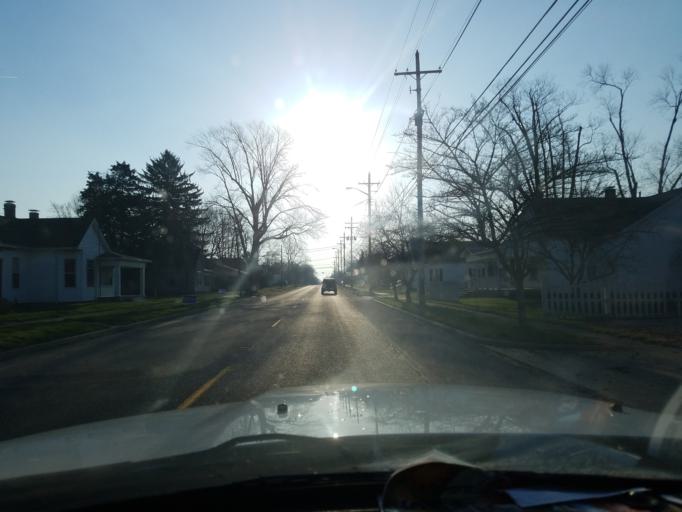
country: US
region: Indiana
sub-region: Vigo County
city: Seelyville
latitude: 39.3903
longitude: -87.3006
